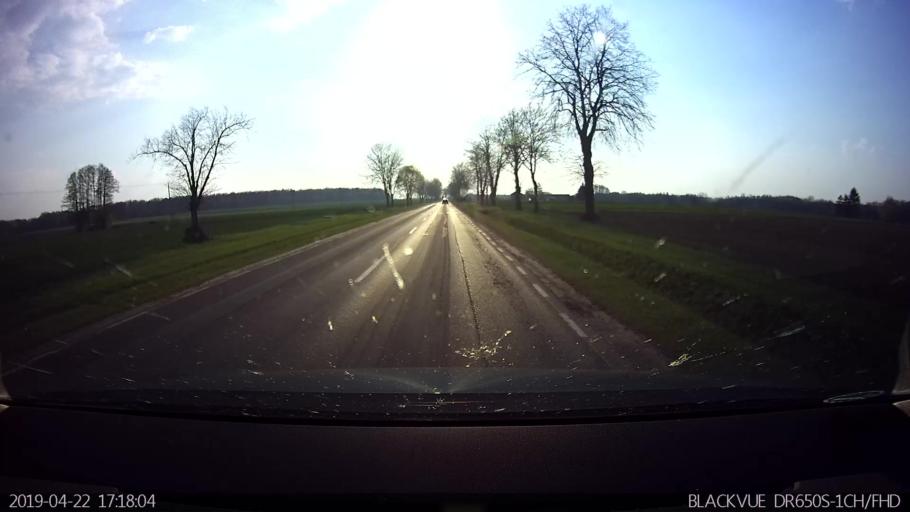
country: PL
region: Masovian Voivodeship
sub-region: Powiat sokolowski
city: Repki
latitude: 52.3855
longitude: 22.4239
